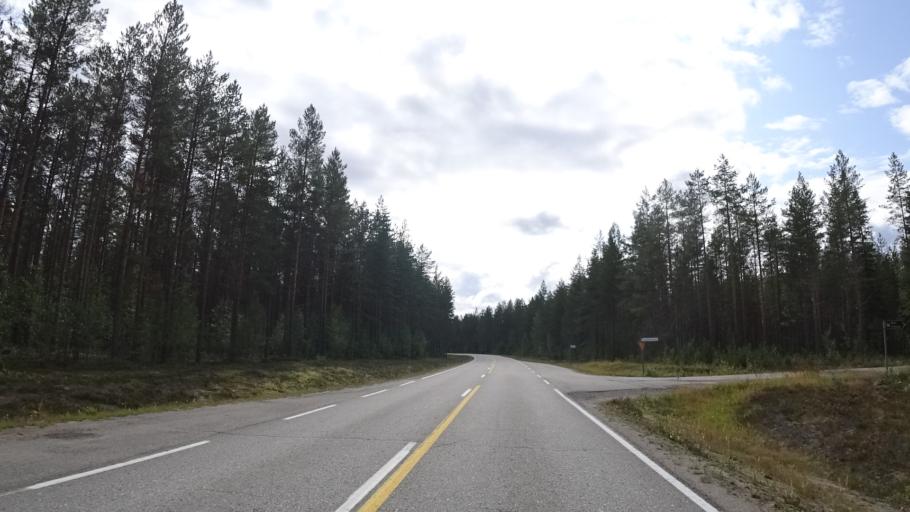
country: FI
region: North Karelia
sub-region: Joensuu
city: Ilomantsi
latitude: 62.7863
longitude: 31.0888
